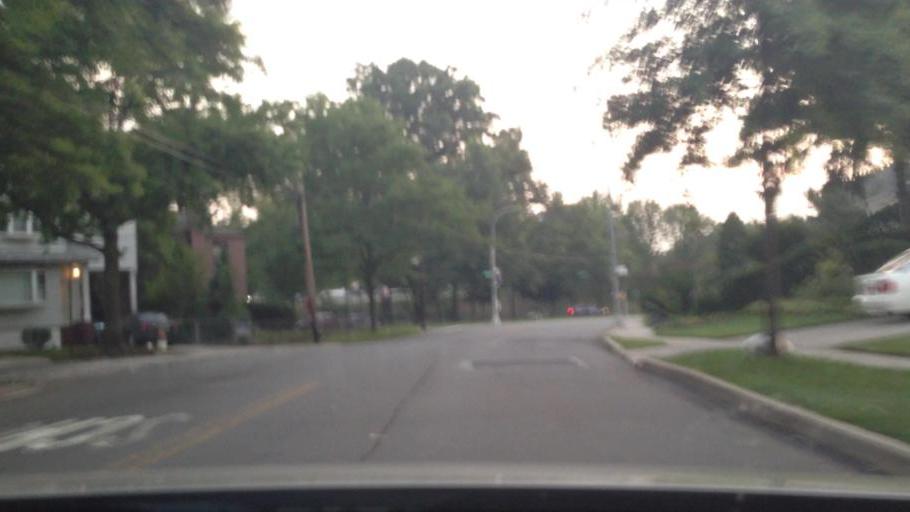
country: US
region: New York
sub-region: Queens County
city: Jamaica
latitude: 40.7178
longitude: -73.7920
